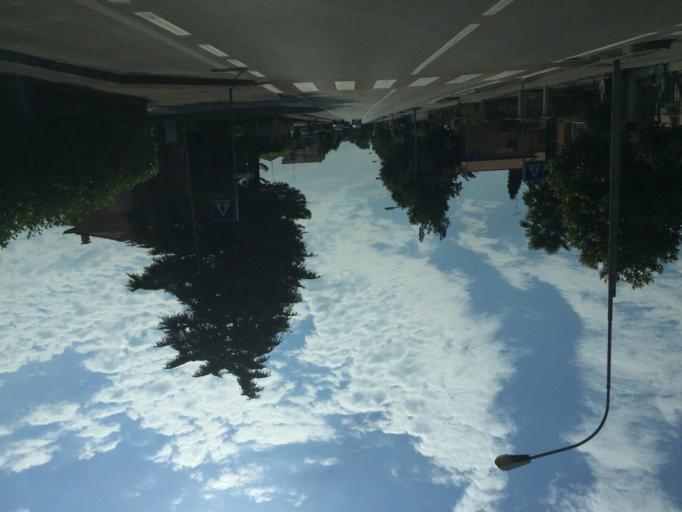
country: IT
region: Friuli Venezia Giulia
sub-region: Provincia di Pordenone
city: Sacile
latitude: 45.9554
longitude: 12.4860
